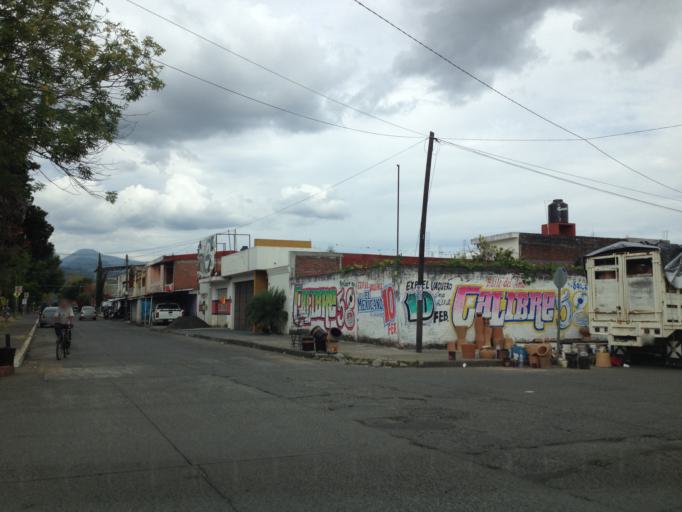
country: MX
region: Michoacan
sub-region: Uruapan
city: Uruapan
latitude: 19.4115
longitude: -102.0380
